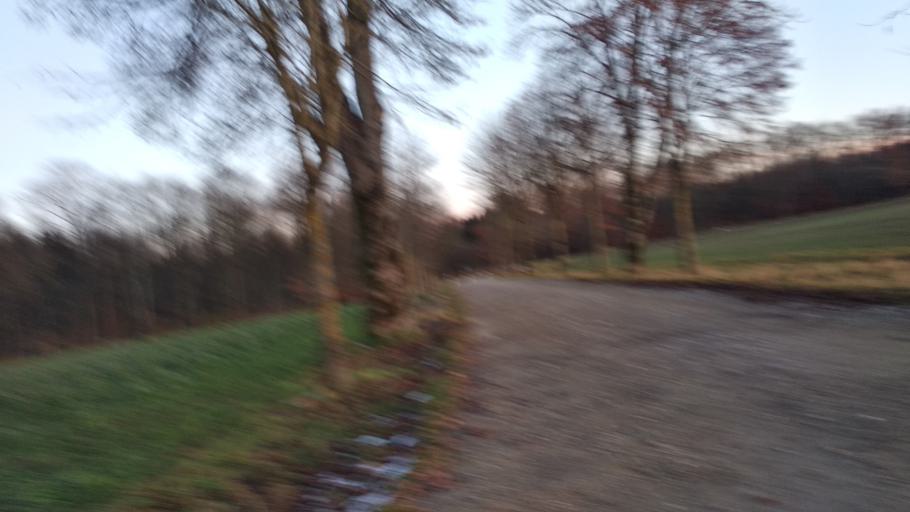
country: DE
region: Bavaria
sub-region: Upper Bavaria
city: Vaterstetten
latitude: 48.0696
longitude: 11.7837
